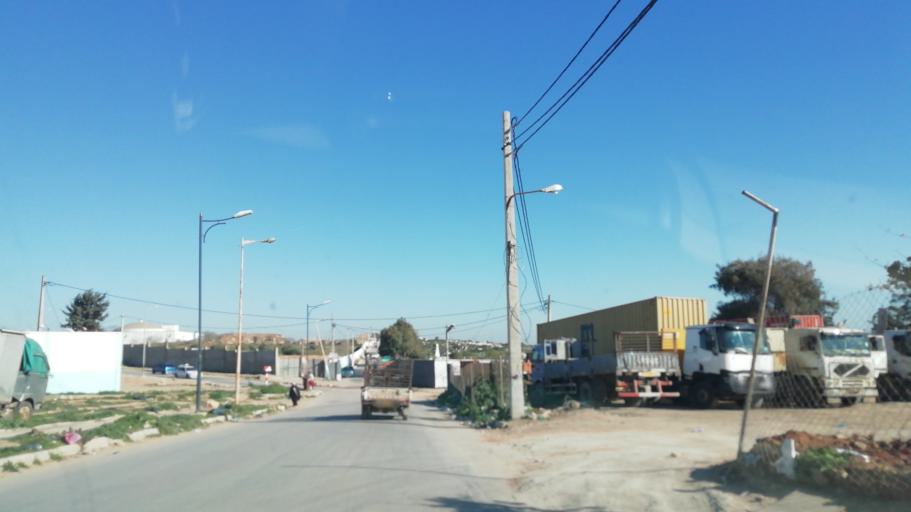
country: DZ
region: Oran
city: Bir el Djir
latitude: 35.7244
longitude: -0.5269
